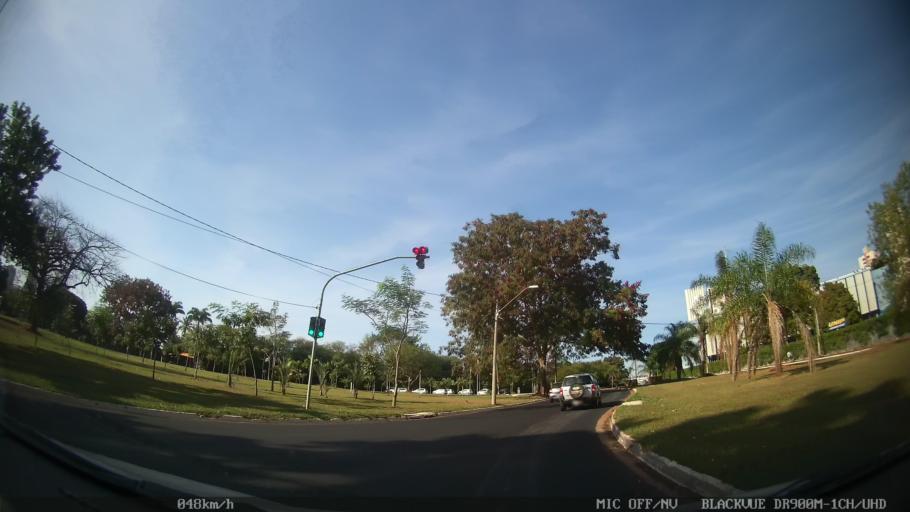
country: BR
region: Sao Paulo
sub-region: Ribeirao Preto
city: Ribeirao Preto
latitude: -21.2181
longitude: -47.8162
